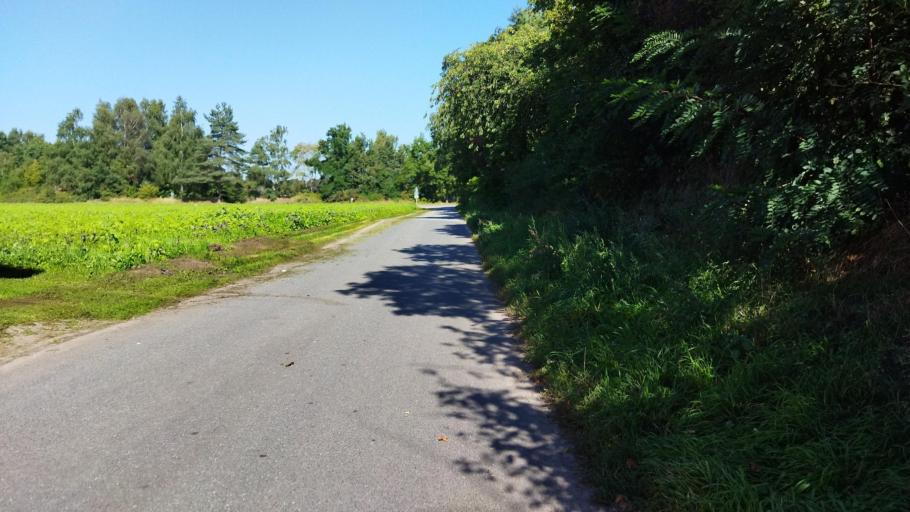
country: DE
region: Lower Saxony
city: Ostercappeln
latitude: 52.3673
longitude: 8.2299
